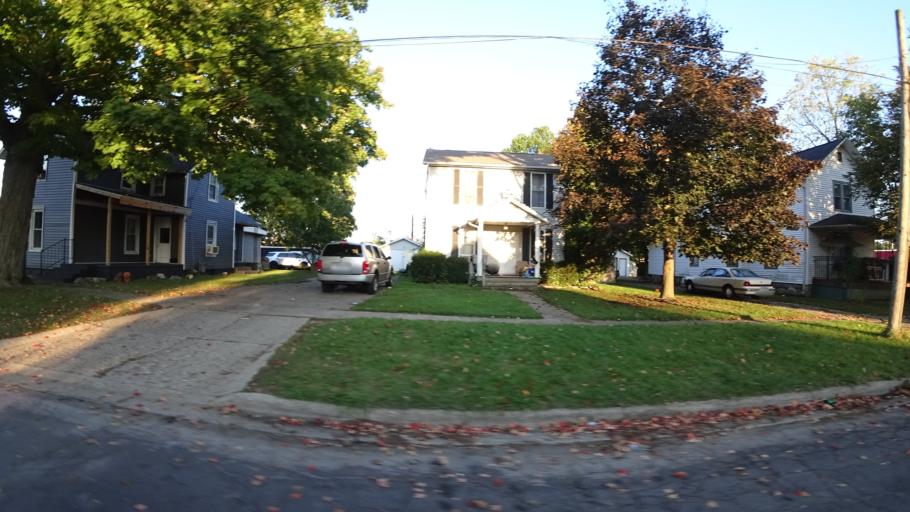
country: US
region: Michigan
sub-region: Saint Joseph County
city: Three Rivers
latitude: 41.9433
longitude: -85.6382
